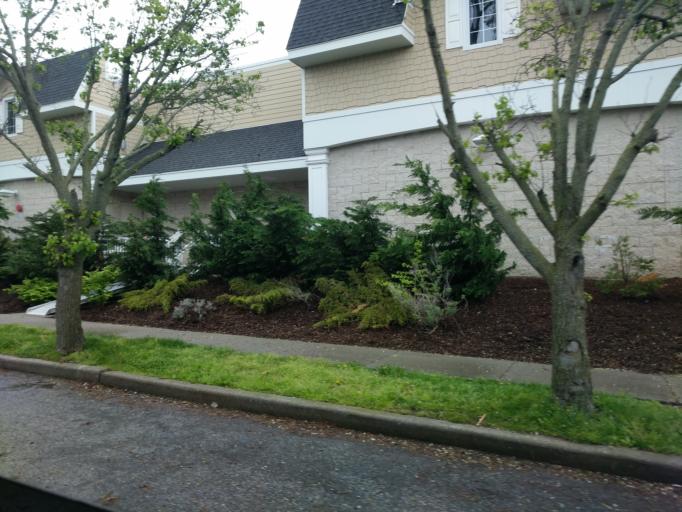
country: US
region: New York
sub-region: Nassau County
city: Island Park
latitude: 40.5980
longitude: -73.6544
